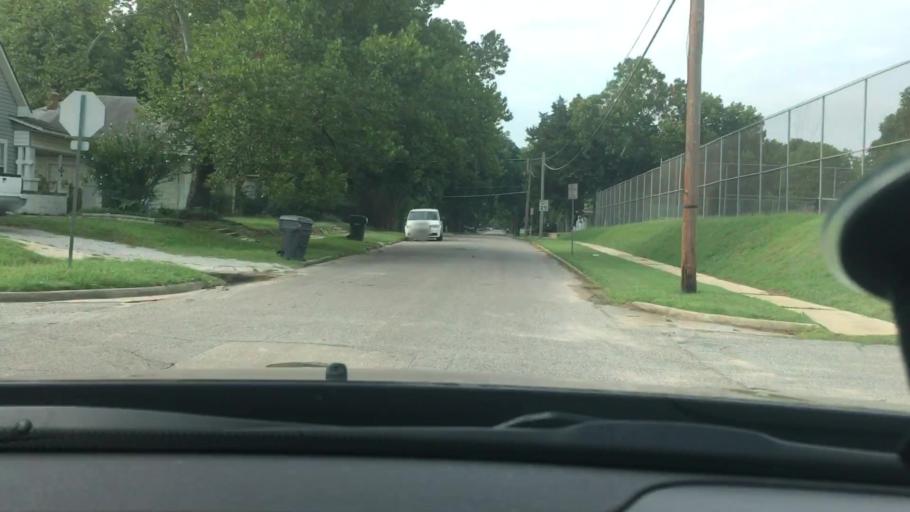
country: US
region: Oklahoma
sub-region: Carter County
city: Ardmore
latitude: 34.1835
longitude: -97.1277
